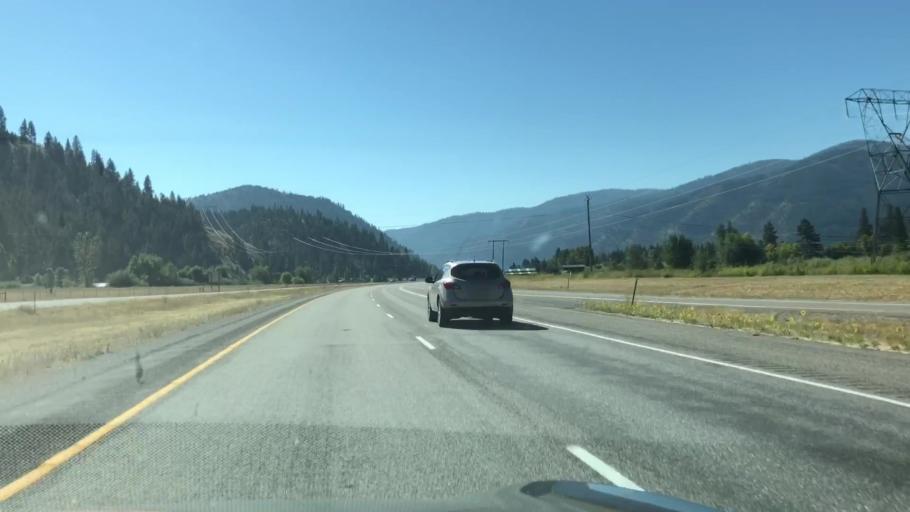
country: US
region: Montana
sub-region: Missoula County
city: Clinton
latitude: 46.7783
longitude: -113.7132
